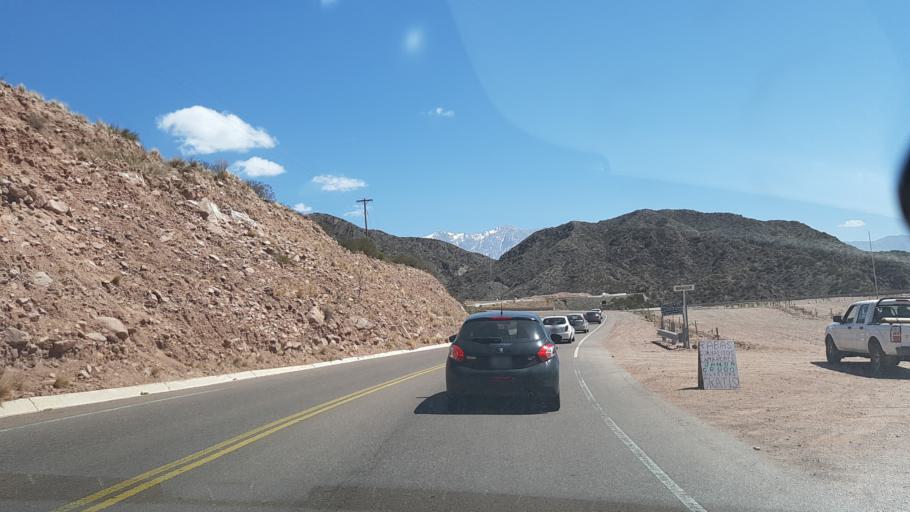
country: AR
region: Mendoza
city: Lujan de Cuyo
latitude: -32.9957
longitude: -69.1438
